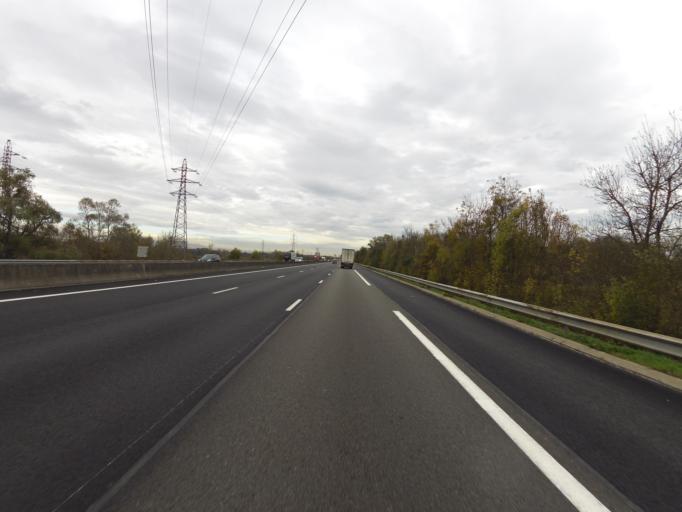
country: FR
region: Rhone-Alpes
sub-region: Departement du Rhone
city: Arnas
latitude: 46.0309
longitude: 4.7257
